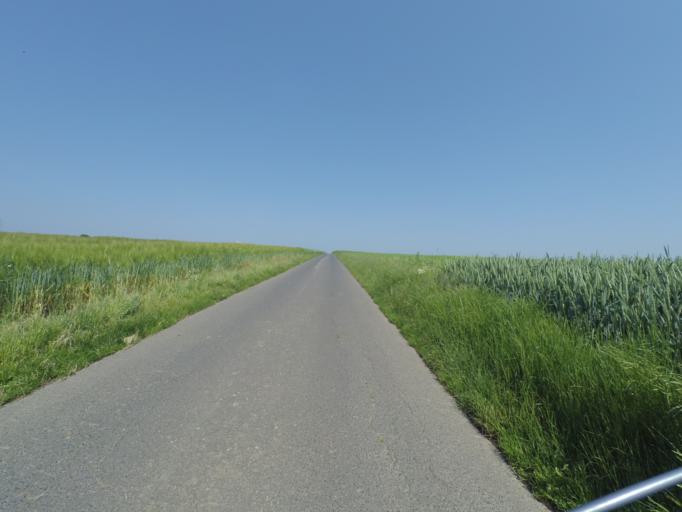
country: DE
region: Rheinland-Pfalz
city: Kollig
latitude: 50.2668
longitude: 7.2733
